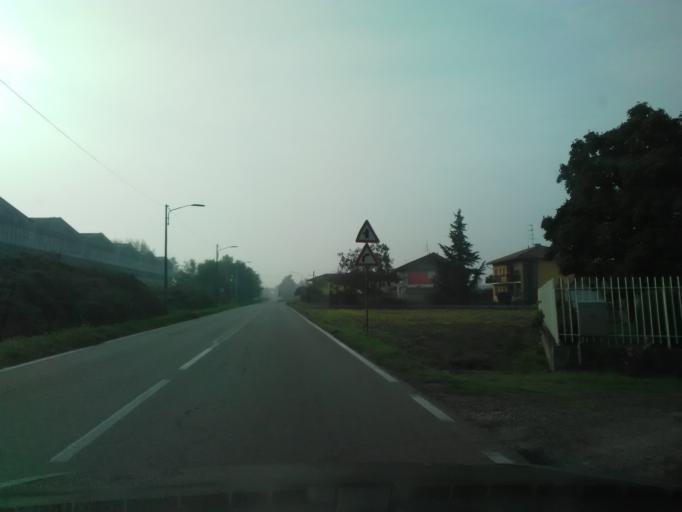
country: IT
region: Piedmont
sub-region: Provincia di Vercelli
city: Santhia
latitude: 45.3589
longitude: 8.1721
